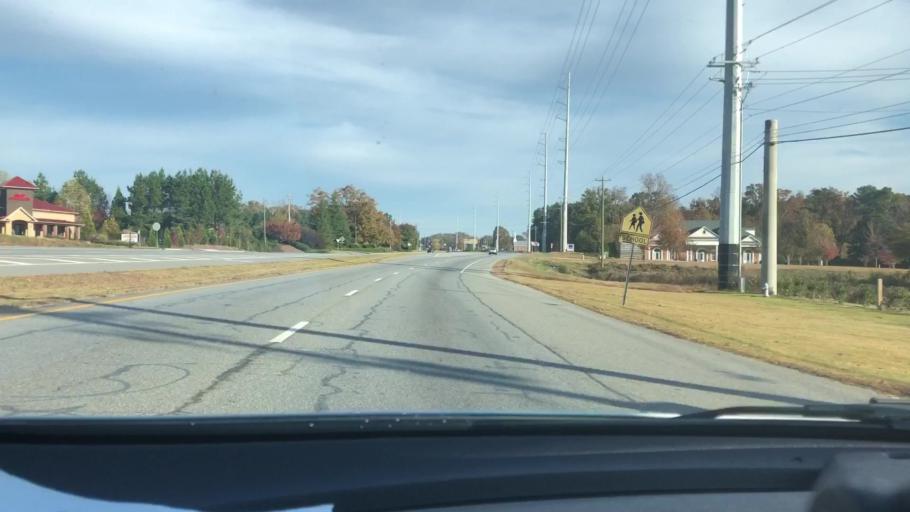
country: US
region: Georgia
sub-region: Forsyth County
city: Cumming
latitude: 34.1358
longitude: -84.1735
